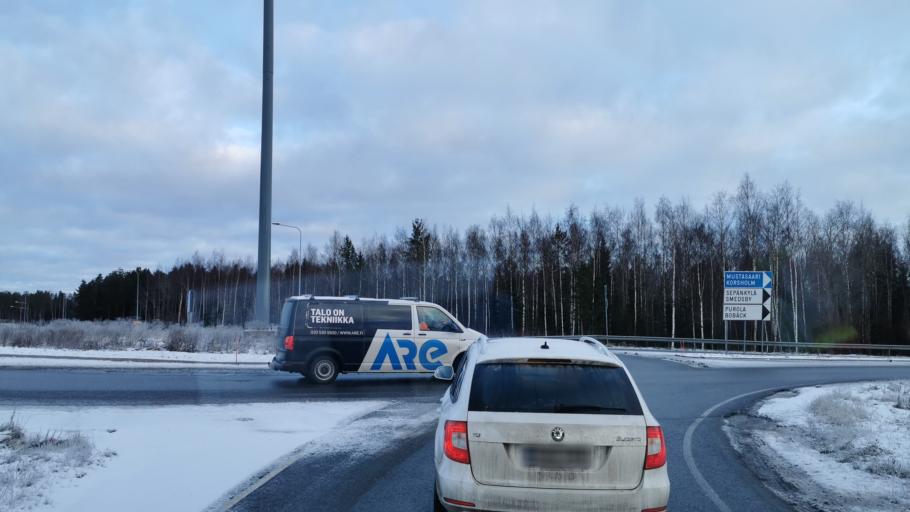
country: FI
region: Ostrobothnia
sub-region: Vaasa
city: Korsholm
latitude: 63.1104
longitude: 21.6636
